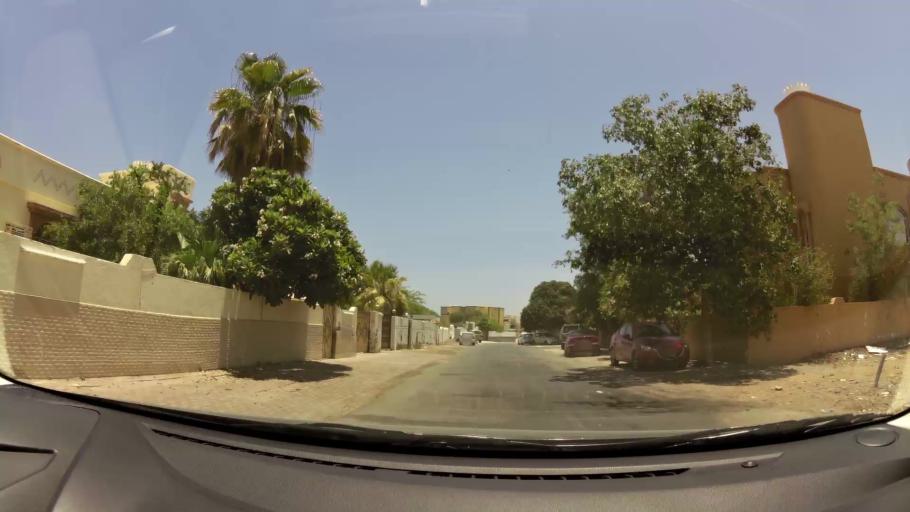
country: OM
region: Muhafazat Masqat
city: As Sib al Jadidah
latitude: 23.6316
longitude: 58.2402
